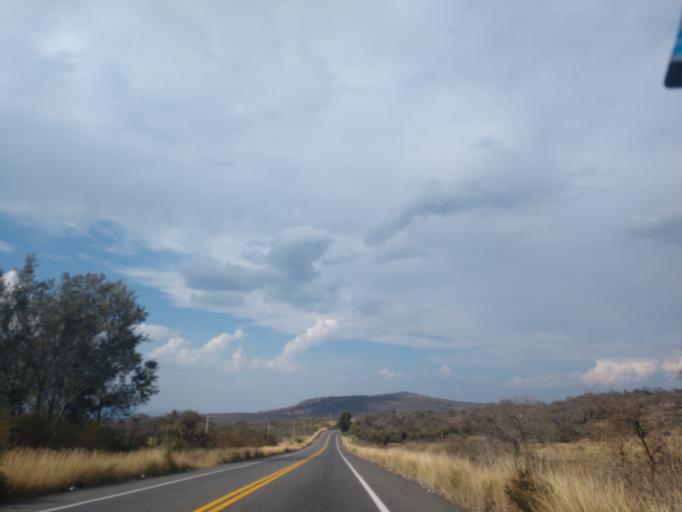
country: MX
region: Jalisco
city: La Manzanilla de la Paz
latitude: 20.0752
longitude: -103.1705
